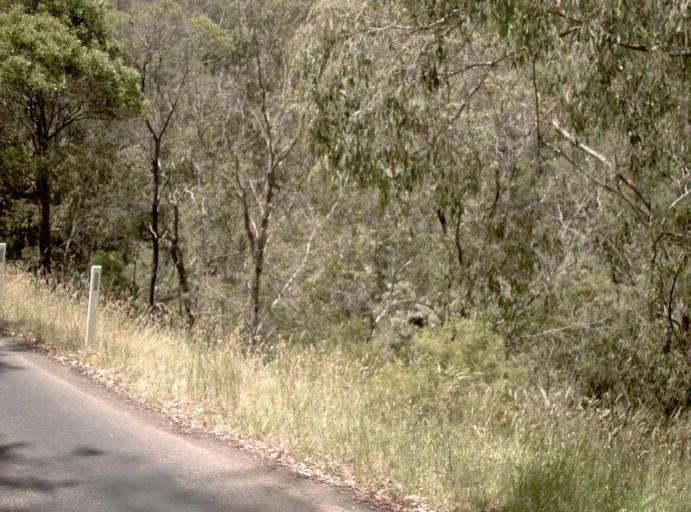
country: AU
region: Victoria
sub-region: Latrobe
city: Traralgon
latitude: -37.9515
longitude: 146.4428
